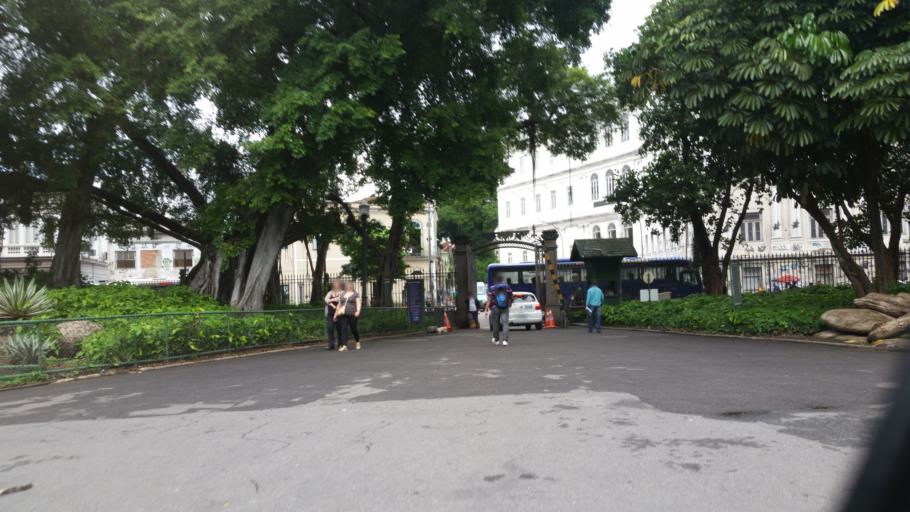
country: BR
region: Rio de Janeiro
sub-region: Rio De Janeiro
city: Rio de Janeiro
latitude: -22.9071
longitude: -43.1898
